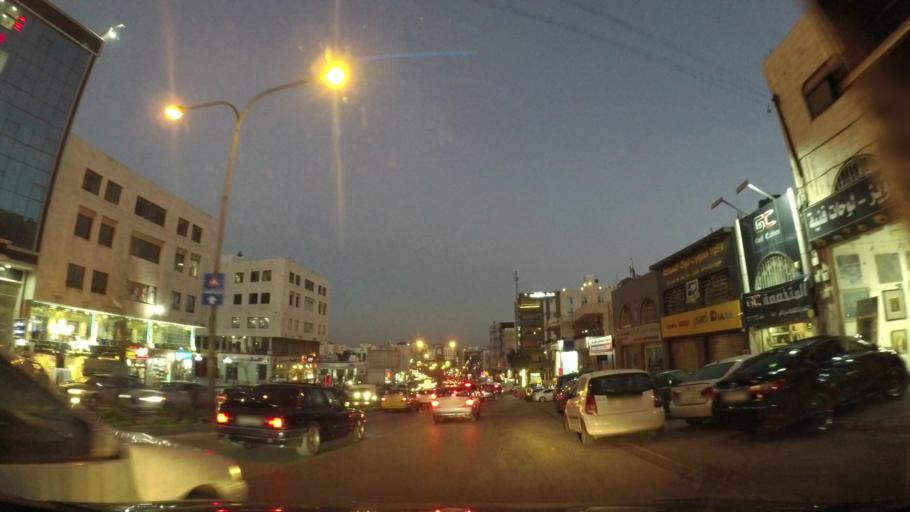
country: JO
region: Amman
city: Al Jubayhah
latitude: 31.9953
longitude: 35.8566
